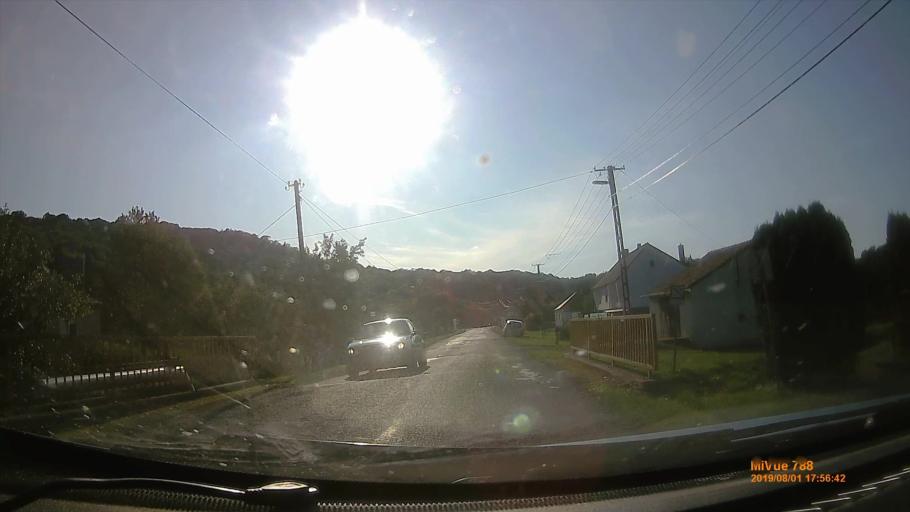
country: HU
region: Baranya
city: Sasd
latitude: 46.1980
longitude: 18.1203
